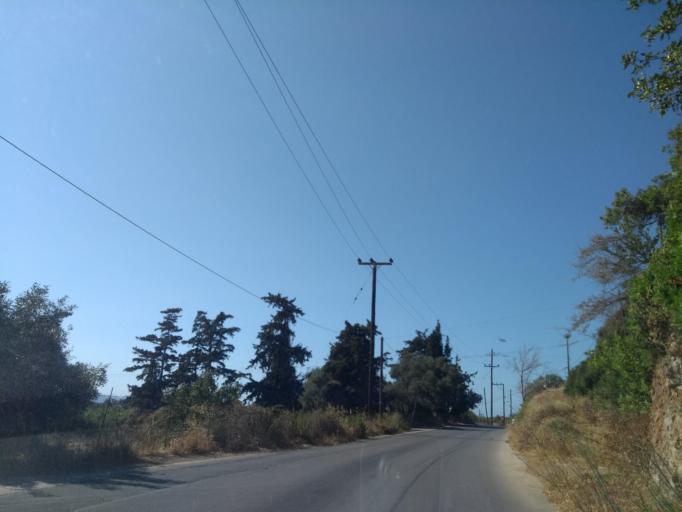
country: GR
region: Crete
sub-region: Nomos Chanias
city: Kissamos
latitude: 35.4978
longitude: 23.7167
